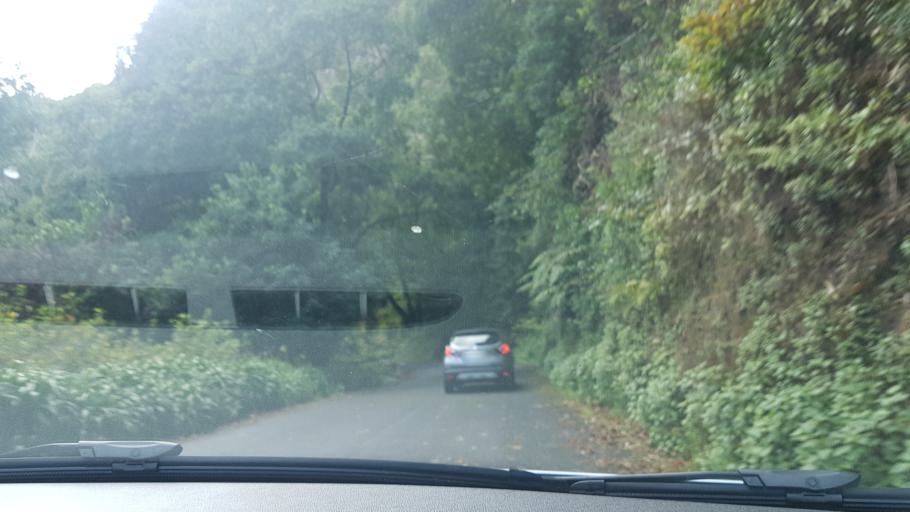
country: PT
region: Madeira
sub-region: Sao Vicente
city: Sao Vicente
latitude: 32.7637
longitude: -17.0268
